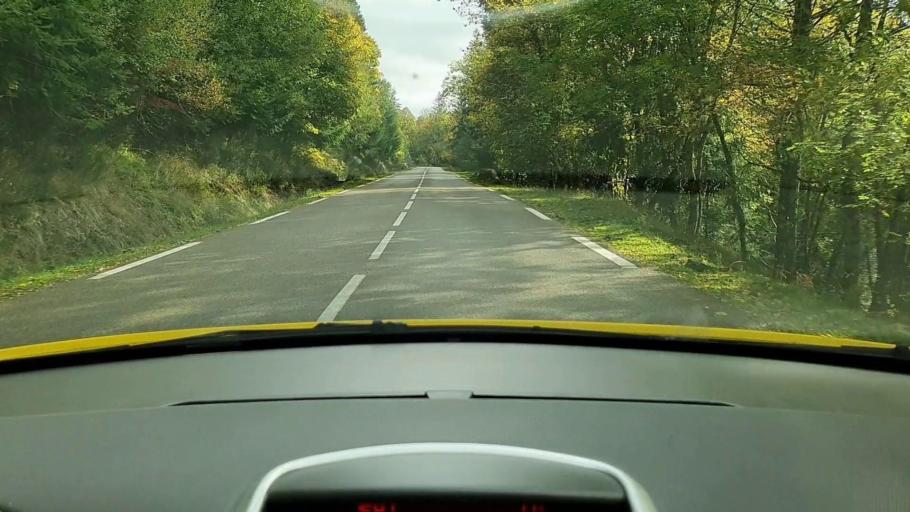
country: FR
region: Languedoc-Roussillon
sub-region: Departement de la Lozere
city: Meyrueis
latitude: 44.1242
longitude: 3.4615
